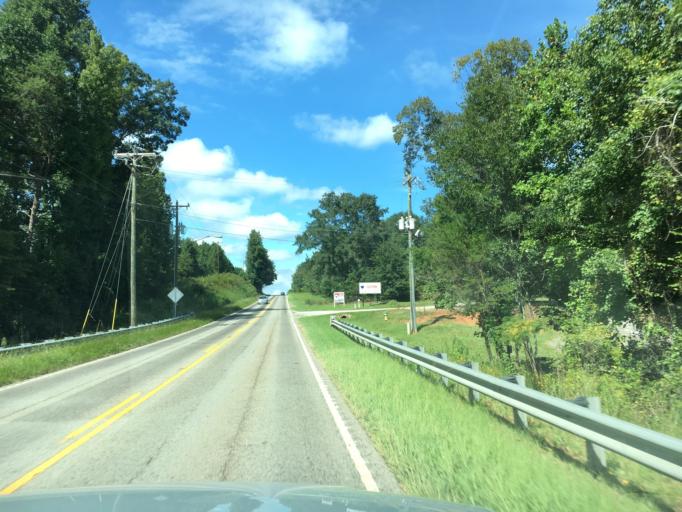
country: US
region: South Carolina
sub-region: Spartanburg County
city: Inman Mills
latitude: 35.0063
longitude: -82.1114
